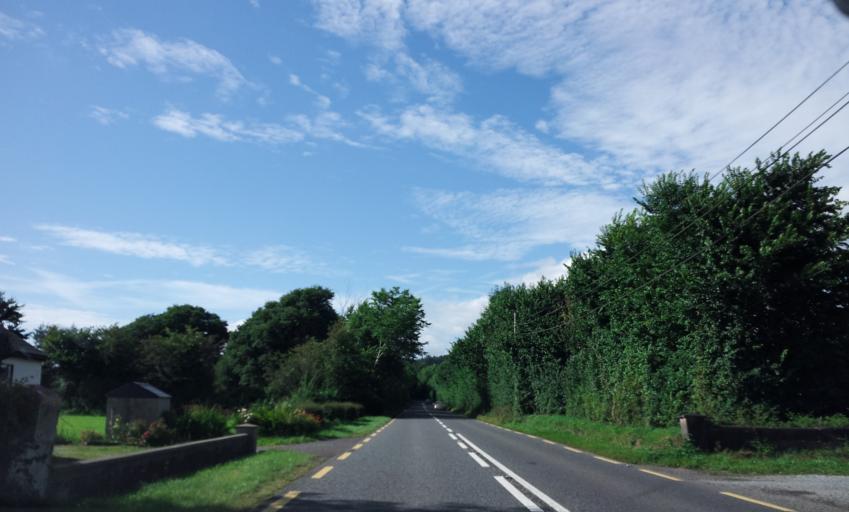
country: IE
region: Munster
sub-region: County Cork
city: Macroom
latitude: 51.9127
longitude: -9.0519
